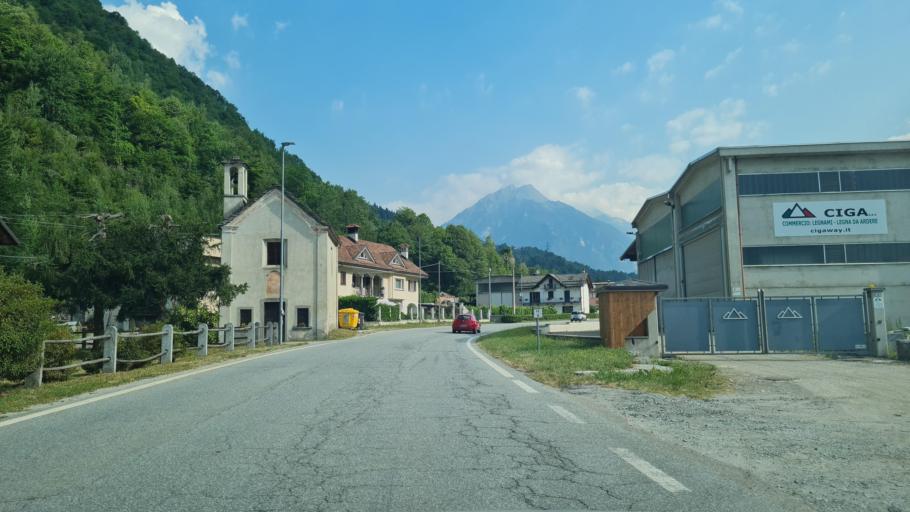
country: IT
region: Piedmont
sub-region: Provincia Verbano-Cusio-Ossola
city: Crodo
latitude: 46.2015
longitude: 8.3177
